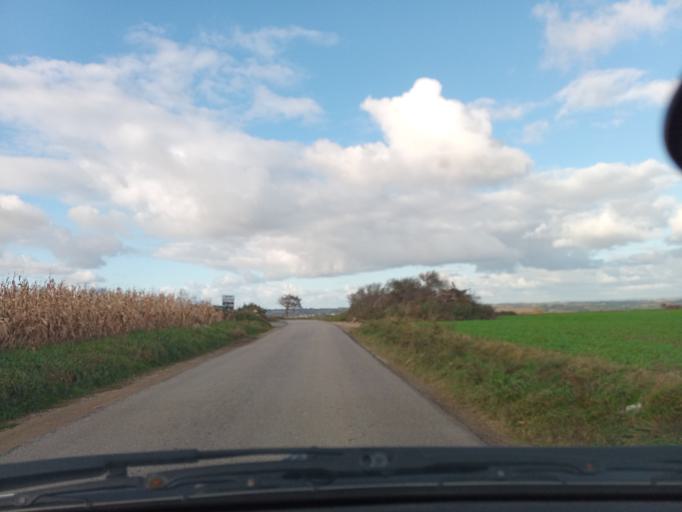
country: FR
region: Brittany
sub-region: Departement du Finistere
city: Plouhinec
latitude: 48.0240
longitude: -4.4982
